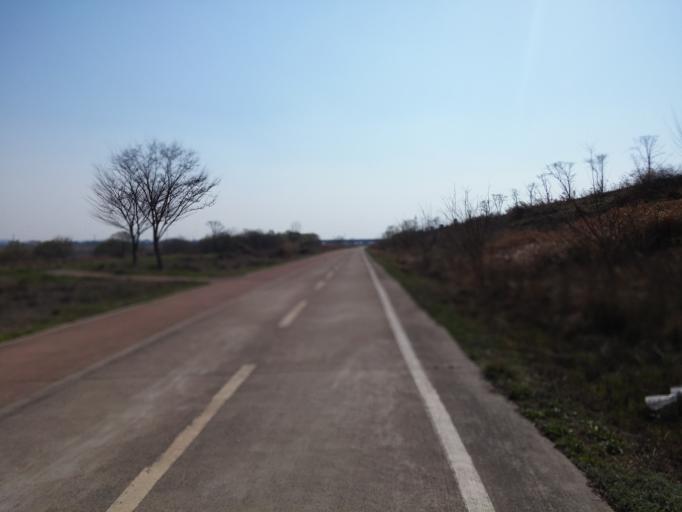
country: KR
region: Chungcheongbuk-do
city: Cheongju-si
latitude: 36.6573
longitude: 127.3800
